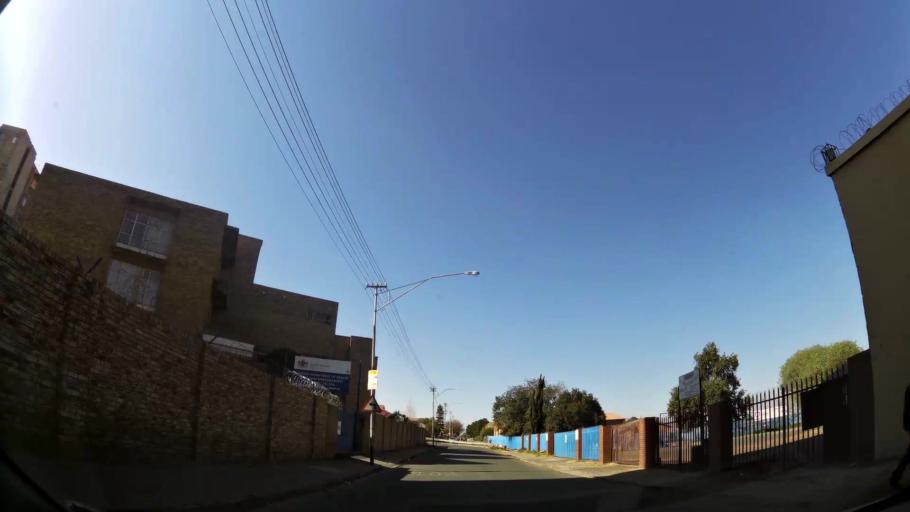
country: ZA
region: Gauteng
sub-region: City of Johannesburg Metropolitan Municipality
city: Johannesburg
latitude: -26.1901
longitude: 27.9723
